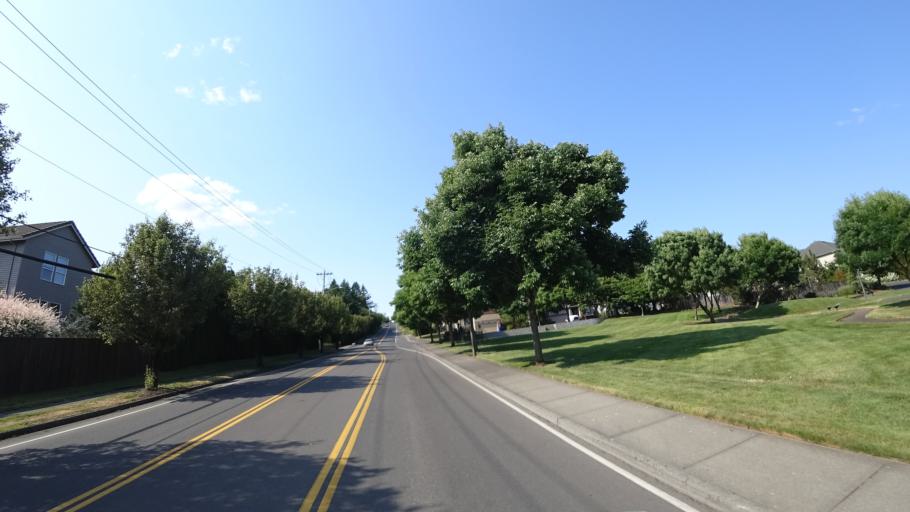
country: US
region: Oregon
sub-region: Clackamas County
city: Happy Valley
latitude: 45.4560
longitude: -122.5141
